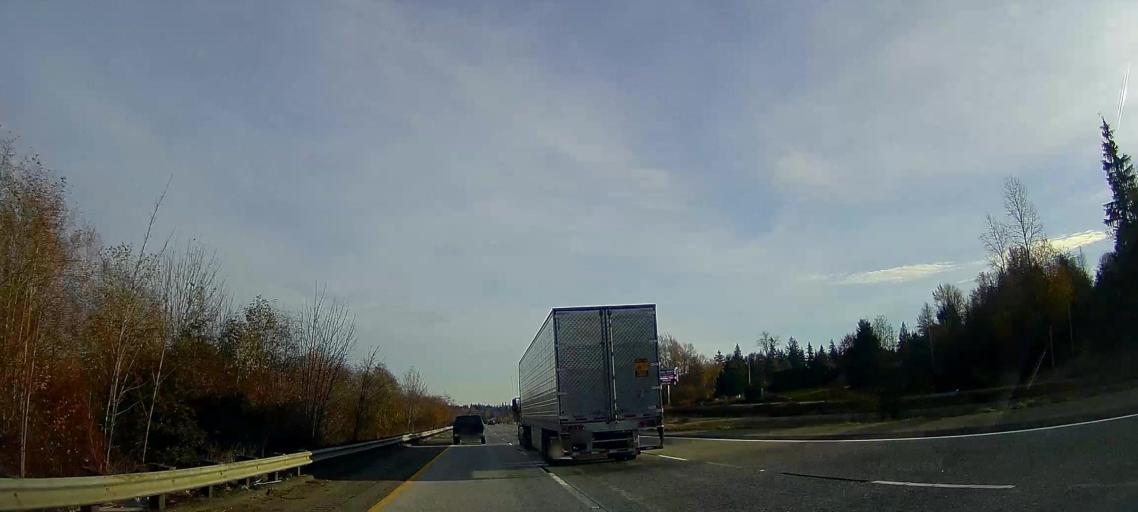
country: US
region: Washington
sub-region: Snohomish County
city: Bryant
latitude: 48.2264
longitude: -122.2286
